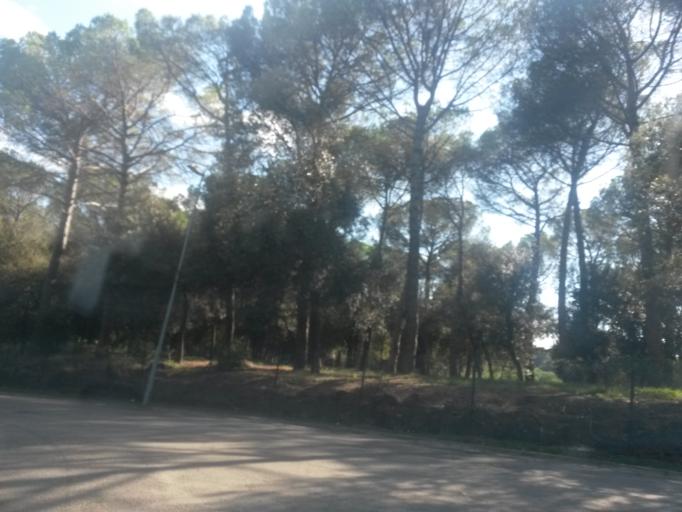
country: ES
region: Catalonia
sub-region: Provincia de Girona
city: Fornells de la Selva
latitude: 41.9484
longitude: 2.8179
